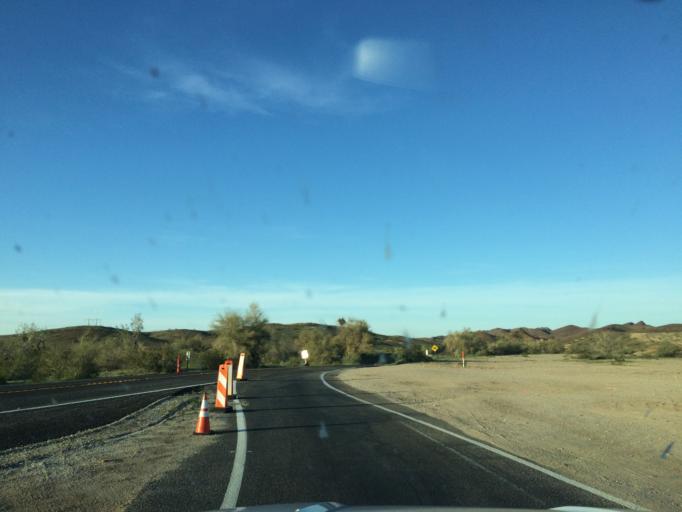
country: MX
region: Baja California
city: Los Algodones
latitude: 33.1364
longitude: -114.8780
